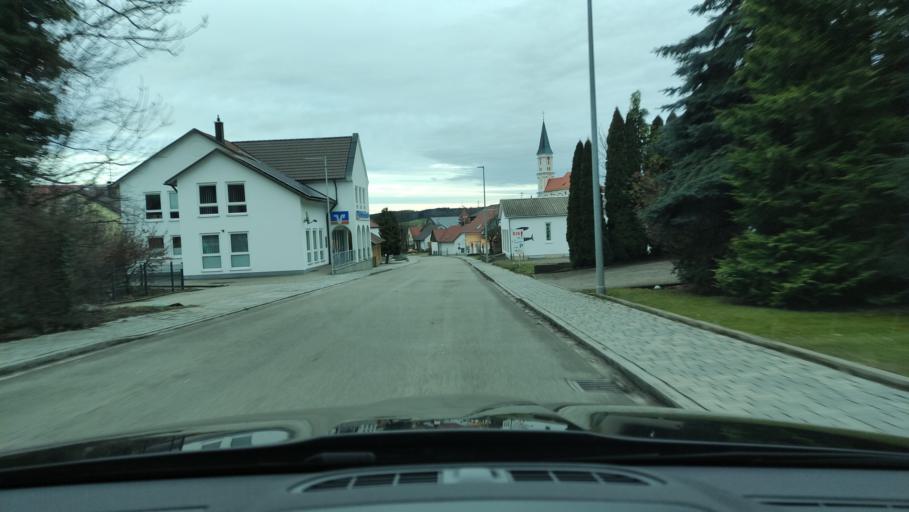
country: DE
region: Bavaria
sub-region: Swabia
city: Breitenthal
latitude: 48.2374
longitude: 10.2961
